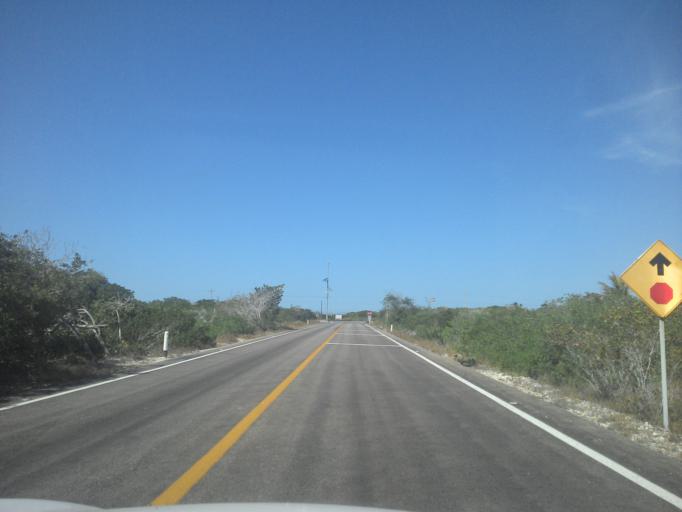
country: MX
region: Yucatan
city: Telchac Puerto
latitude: 21.3316
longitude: -89.3487
